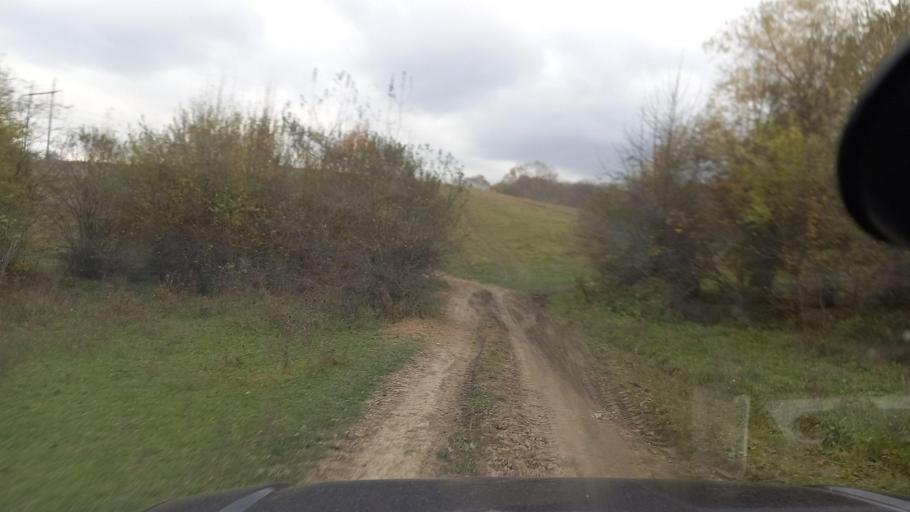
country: RU
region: Krasnodarskiy
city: Gubskaya
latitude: 44.2937
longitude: 40.5532
